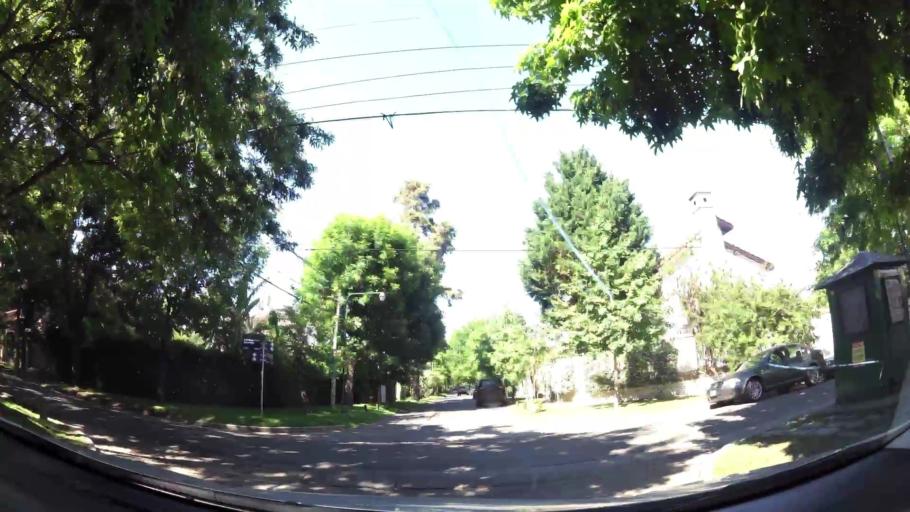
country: AR
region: Buenos Aires
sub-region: Partido de Tigre
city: Tigre
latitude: -34.4804
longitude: -58.5776
